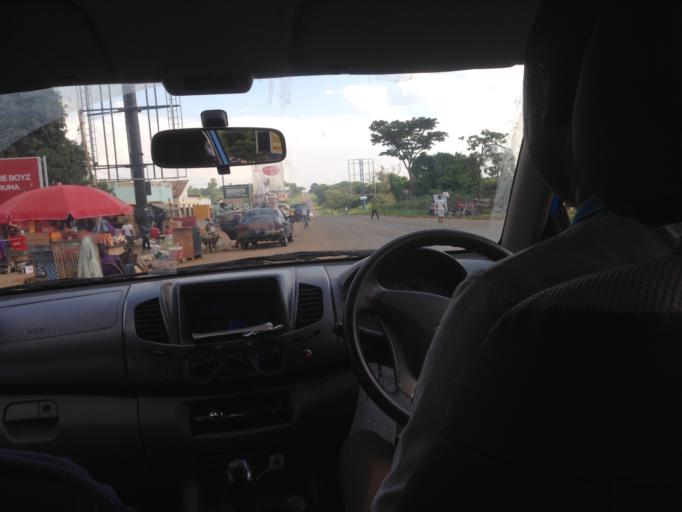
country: UG
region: Northern Region
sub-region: Oyam District
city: Oyam
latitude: 2.2345
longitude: 32.2462
